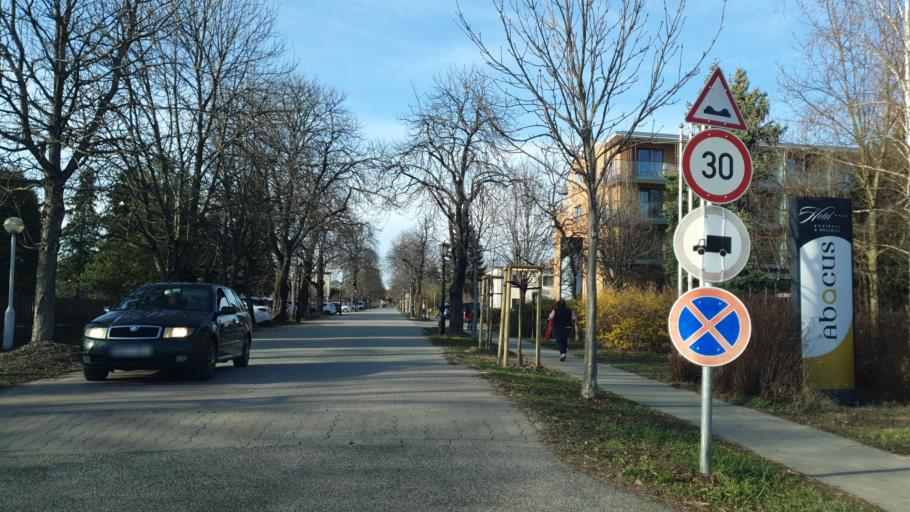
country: HU
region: Fejer
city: Etyek
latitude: 47.4995
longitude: 18.7527
